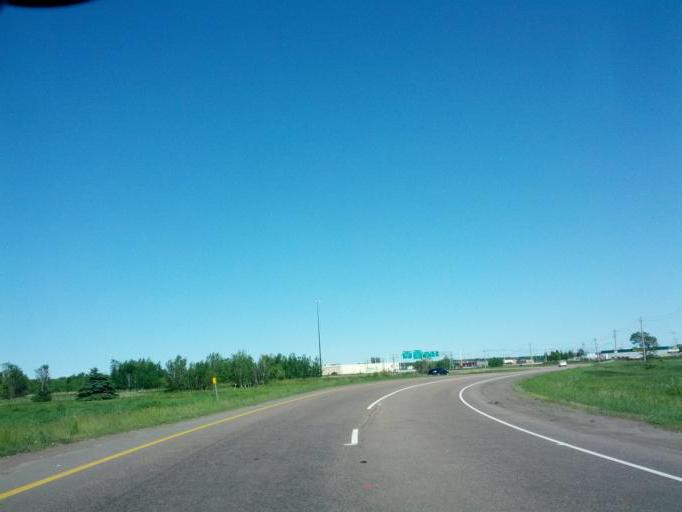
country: CA
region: New Brunswick
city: Moncton
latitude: 46.0971
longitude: -64.7706
